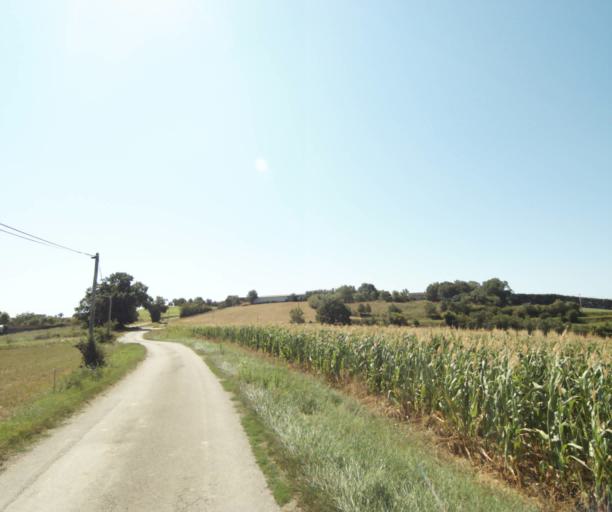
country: FR
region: Midi-Pyrenees
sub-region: Departement de l'Ariege
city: Lezat-sur-Leze
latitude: 43.2540
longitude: 1.4040
